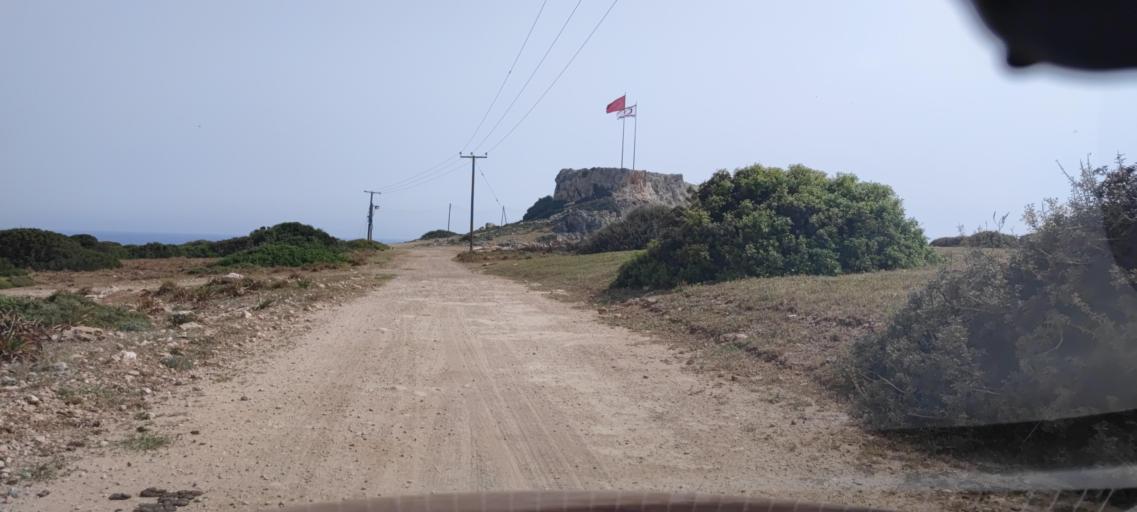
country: CY
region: Ammochostos
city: Rizokarpaso
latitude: 35.6932
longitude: 34.5853
